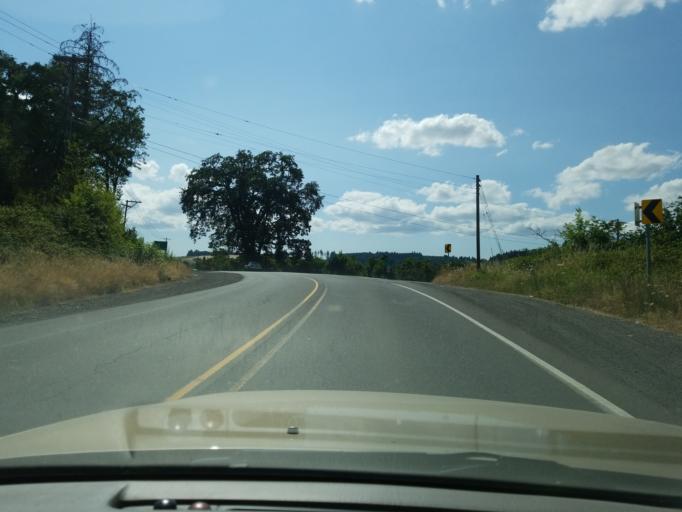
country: US
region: Oregon
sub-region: Yamhill County
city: Dundee
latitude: 45.3211
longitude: -123.0782
